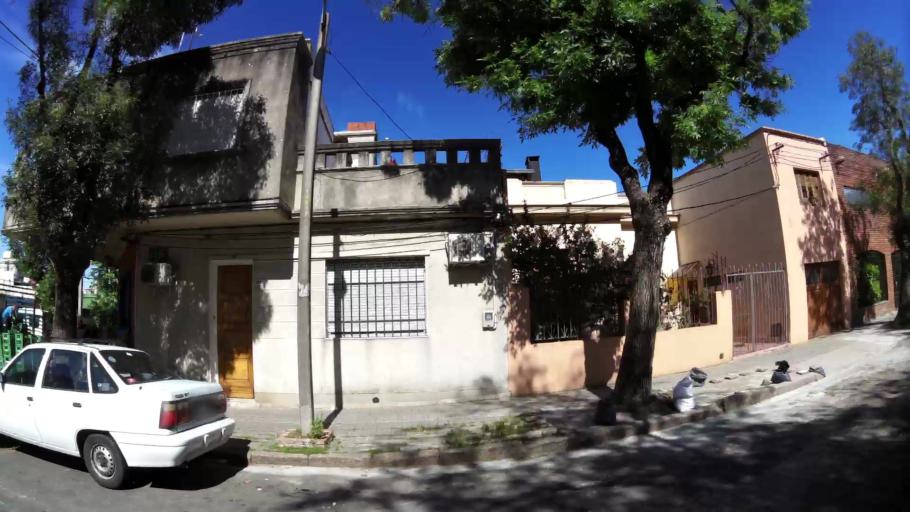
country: UY
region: Montevideo
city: Montevideo
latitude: -34.9002
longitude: -56.1491
